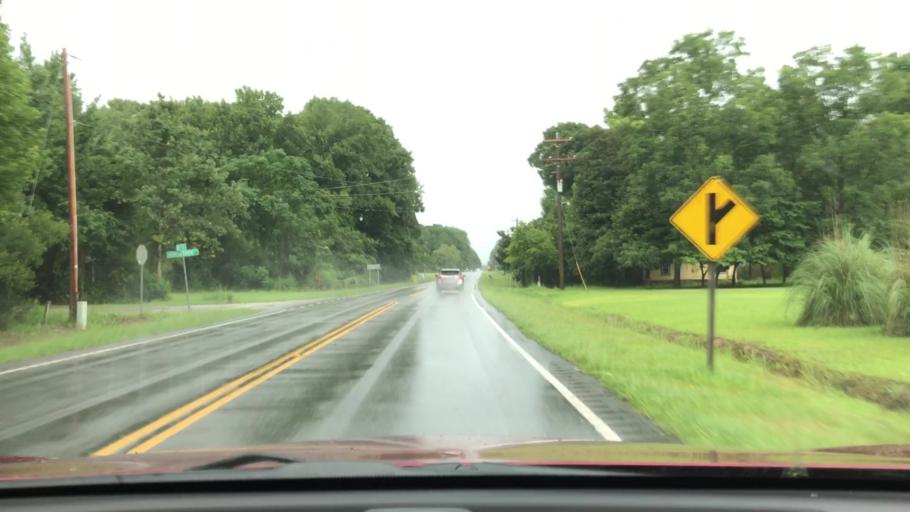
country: US
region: South Carolina
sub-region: Horry County
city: Socastee
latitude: 33.6990
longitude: -79.1103
